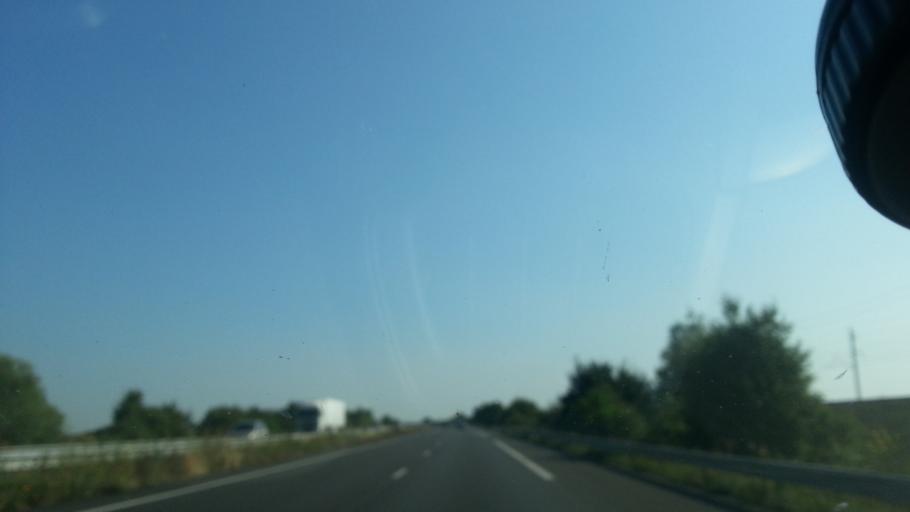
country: FR
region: Centre
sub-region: Departement d'Indre-et-Loire
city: La Celle-Saint-Avant
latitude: 47.0412
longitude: 0.5804
